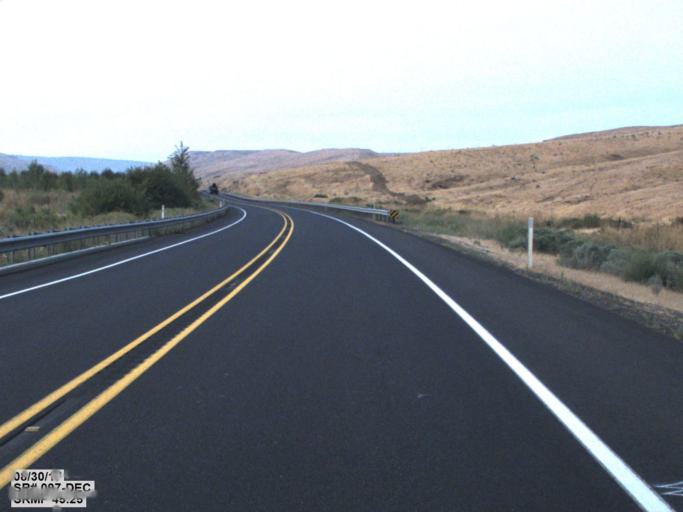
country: US
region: Washington
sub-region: Yakima County
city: Toppenish
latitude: 46.1979
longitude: -120.4872
